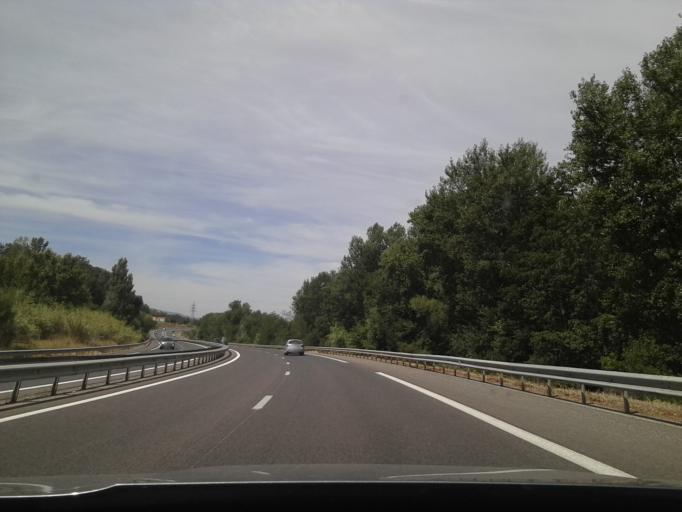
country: FR
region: Languedoc-Roussillon
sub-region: Departement des Pyrenees-Orientales
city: Le Soler
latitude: 42.6841
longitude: 2.7865
